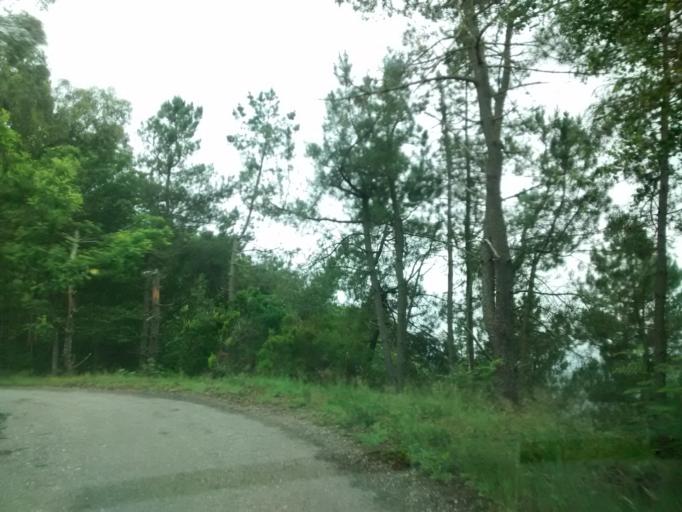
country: ES
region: Galicia
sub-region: Provincia de Ourense
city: Castro Caldelas
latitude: 42.4075
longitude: -7.3937
